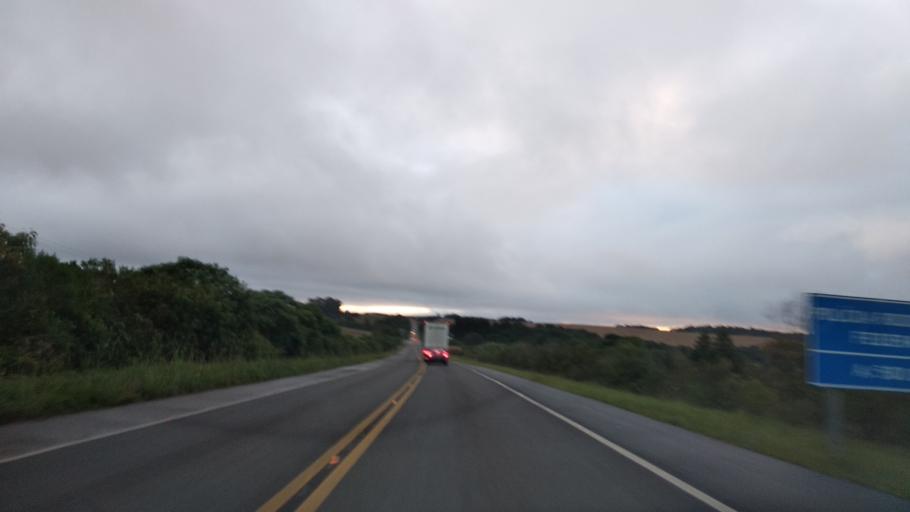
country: BR
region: Santa Catarina
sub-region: Campos Novos
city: Campos Novos
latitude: -27.3894
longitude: -51.1203
